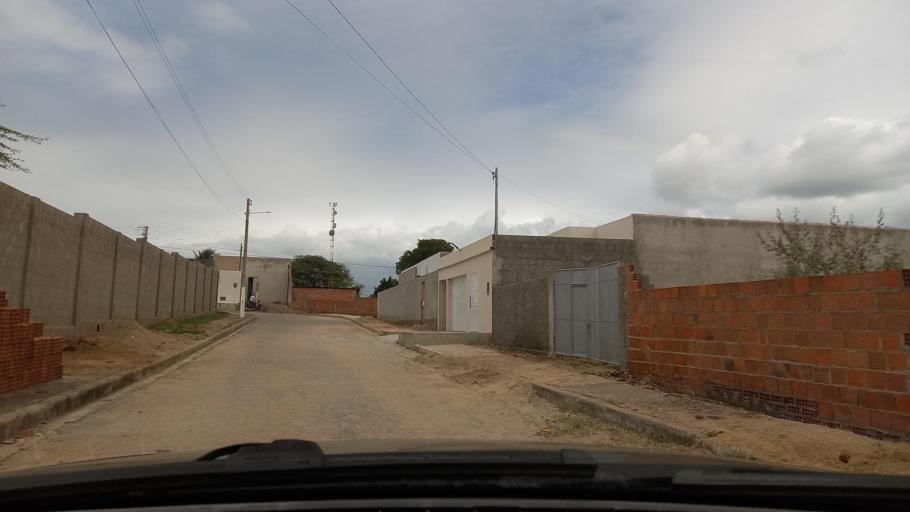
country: BR
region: Sergipe
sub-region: Caninde De Sao Francisco
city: Caninde de Sao Francisco
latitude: -9.6128
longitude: -37.7653
